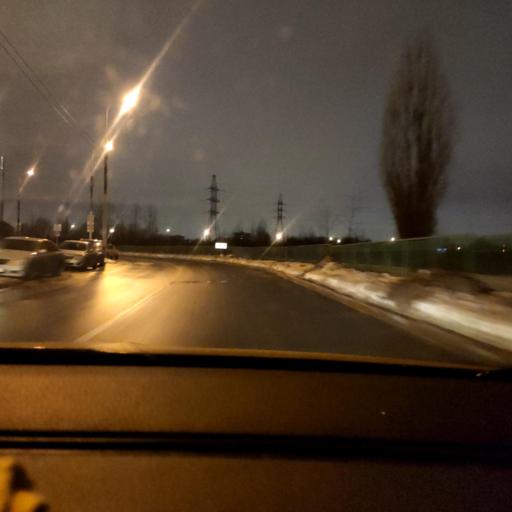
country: RU
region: Moscow
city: Zhulebino
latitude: 55.7172
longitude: 37.8799
